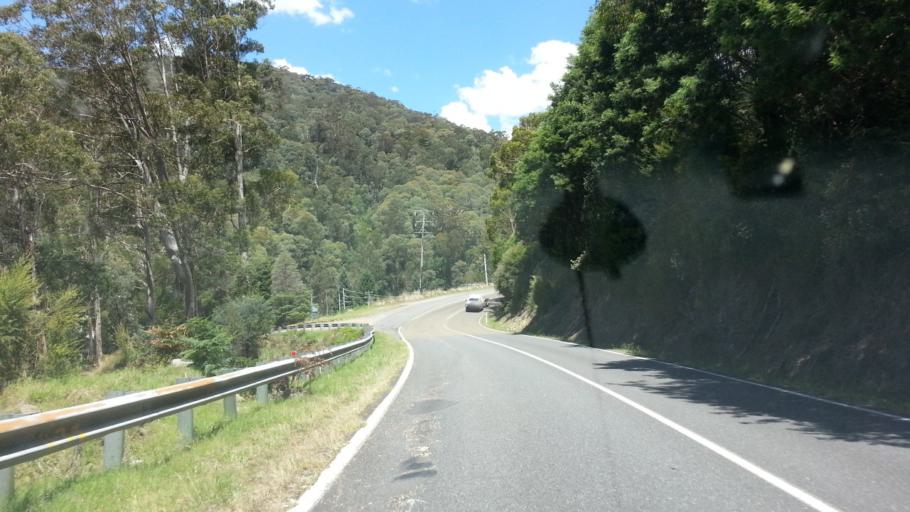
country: AU
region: Victoria
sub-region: Alpine
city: Mount Beauty
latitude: -36.7835
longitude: 147.2181
